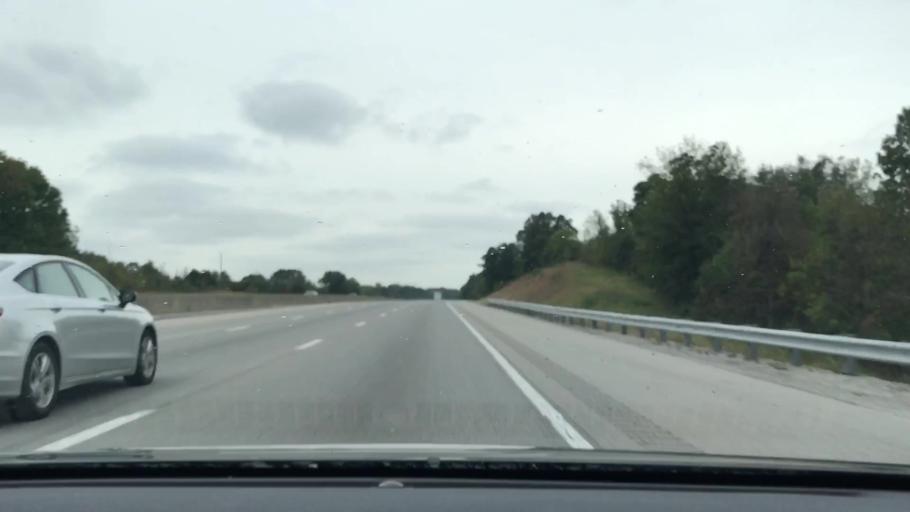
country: US
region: Kentucky
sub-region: Simpson County
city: Franklin
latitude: 36.7612
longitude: -86.4868
